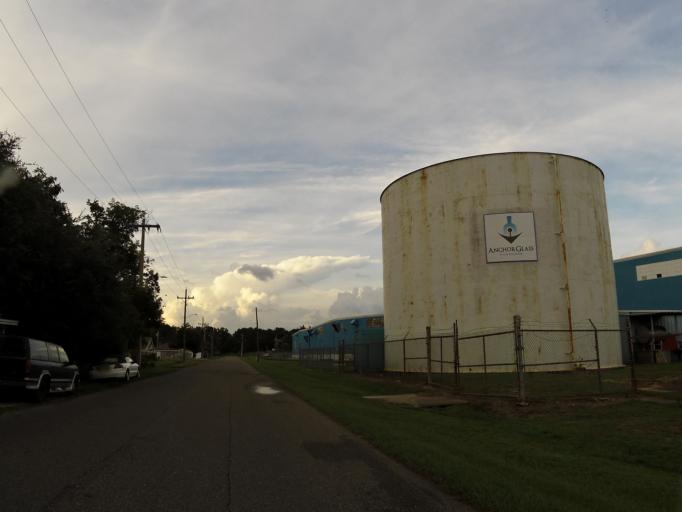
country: US
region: Florida
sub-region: Duval County
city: Jacksonville
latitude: 30.3485
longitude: -81.7141
